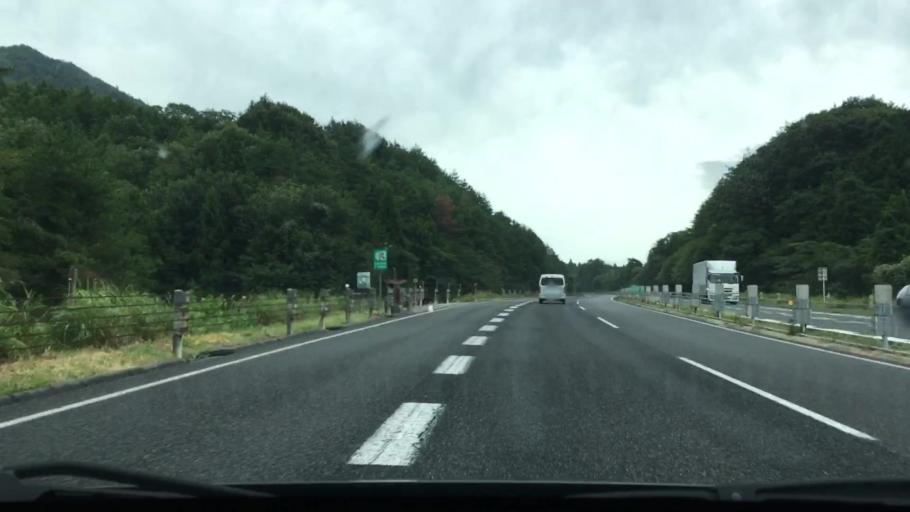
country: JP
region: Hiroshima
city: Hiroshima-shi
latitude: 34.6321
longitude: 132.5134
